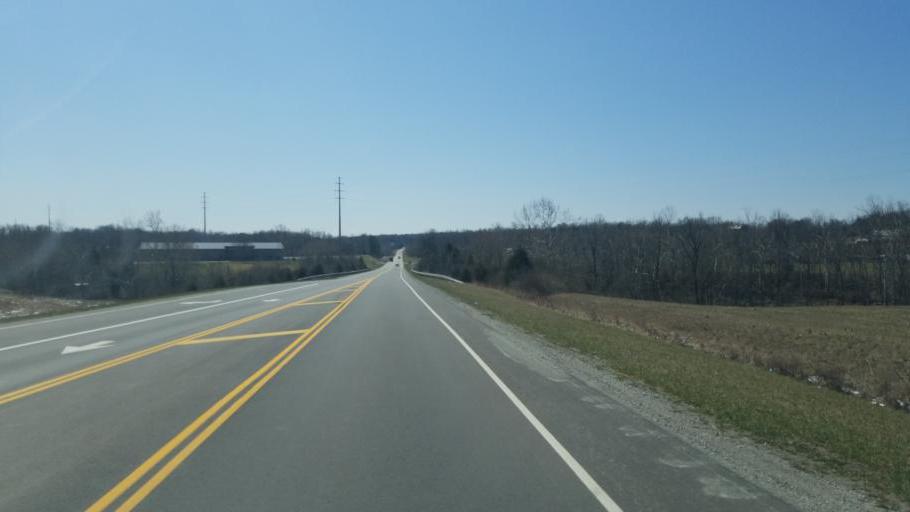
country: US
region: Ohio
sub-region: Highland County
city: Hillsboro
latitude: 39.1855
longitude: -83.6170
